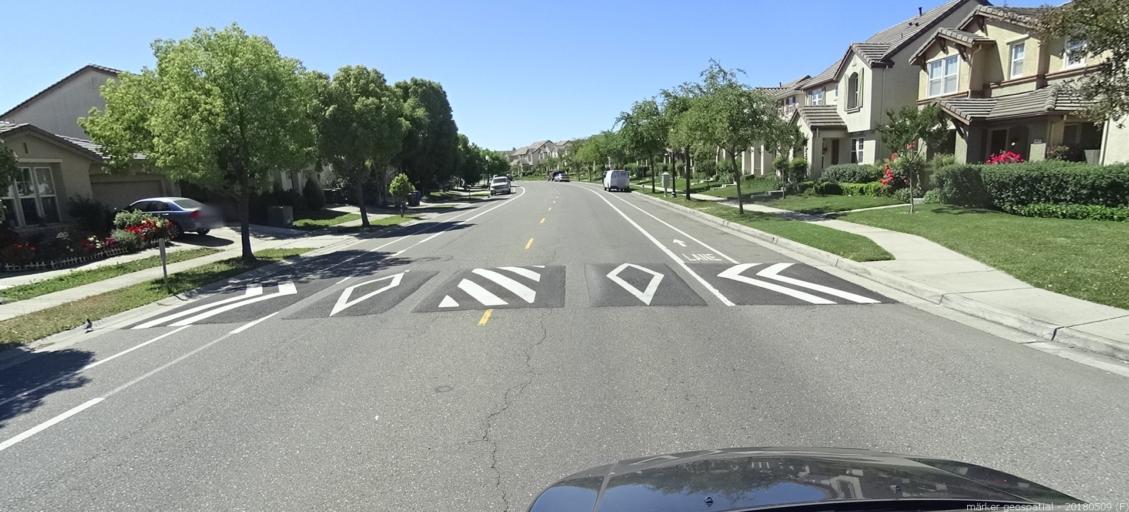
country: US
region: California
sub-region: Yolo County
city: West Sacramento
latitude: 38.6636
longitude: -121.5293
